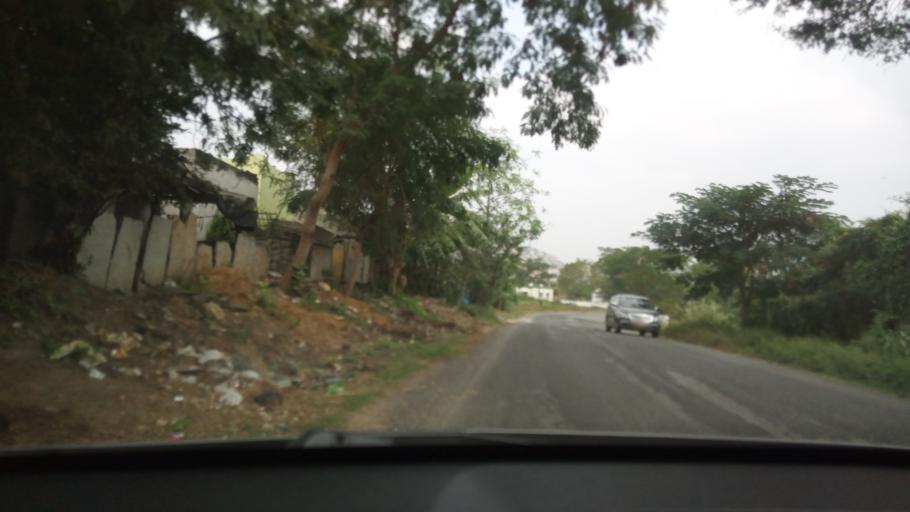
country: IN
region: Andhra Pradesh
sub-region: Chittoor
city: Pakala
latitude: 13.6562
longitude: 78.8416
